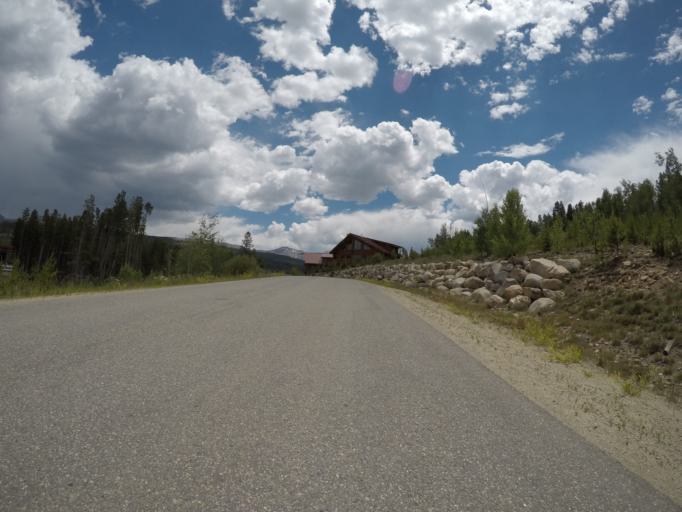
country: US
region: Colorado
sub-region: Grand County
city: Fraser
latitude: 39.9252
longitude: -105.7895
